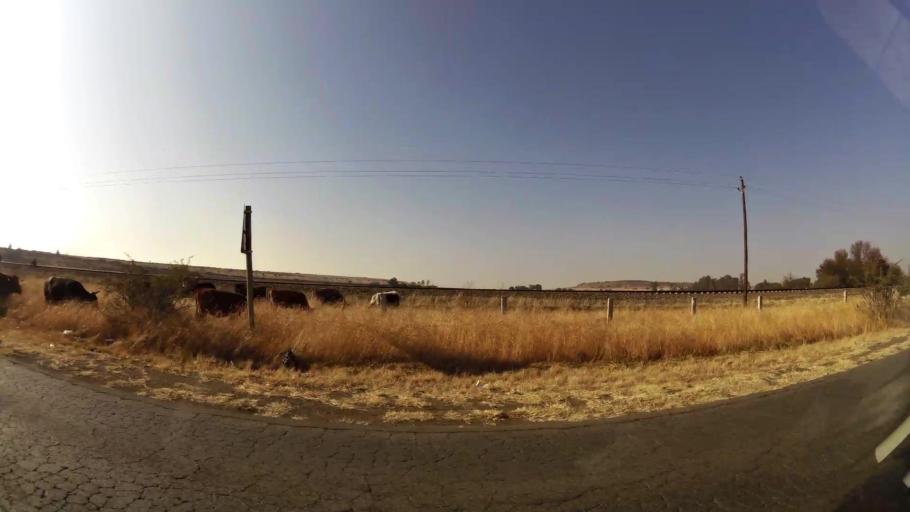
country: ZA
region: Orange Free State
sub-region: Mangaung Metropolitan Municipality
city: Bloemfontein
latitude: -29.1833
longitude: 26.1878
